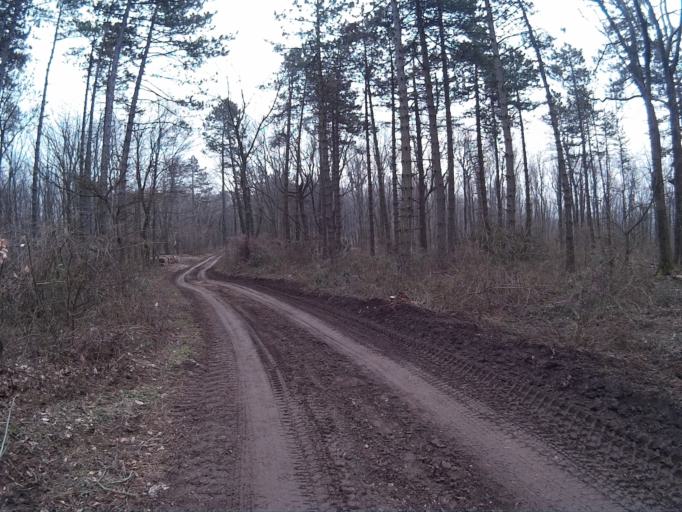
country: HU
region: Veszprem
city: Zirc
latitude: 47.1845
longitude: 17.8384
